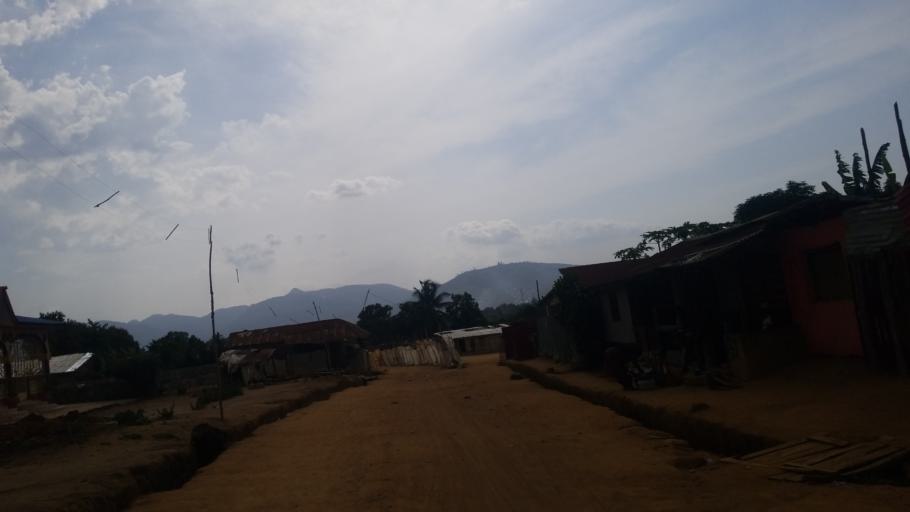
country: SL
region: Western Area
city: Waterloo
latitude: 8.3208
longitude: -13.0485
